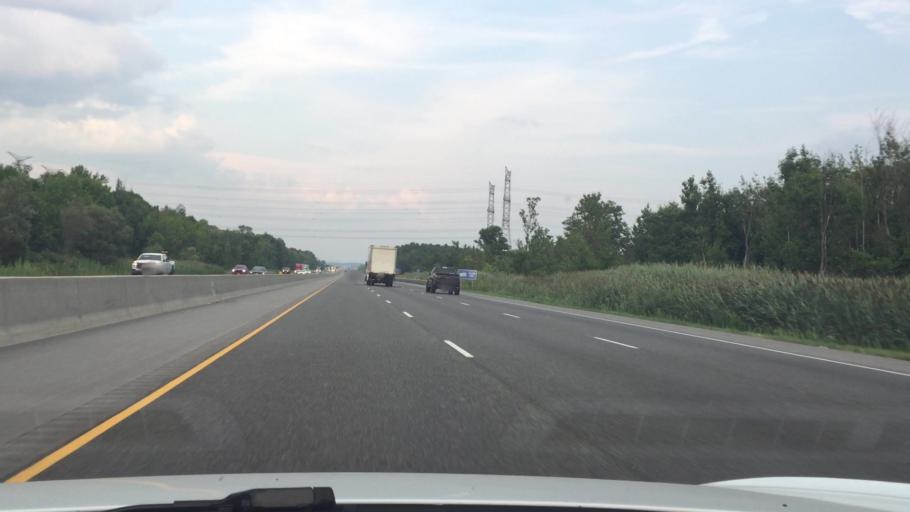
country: CA
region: Ontario
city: Cobourg
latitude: 43.9461
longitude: -78.4214
